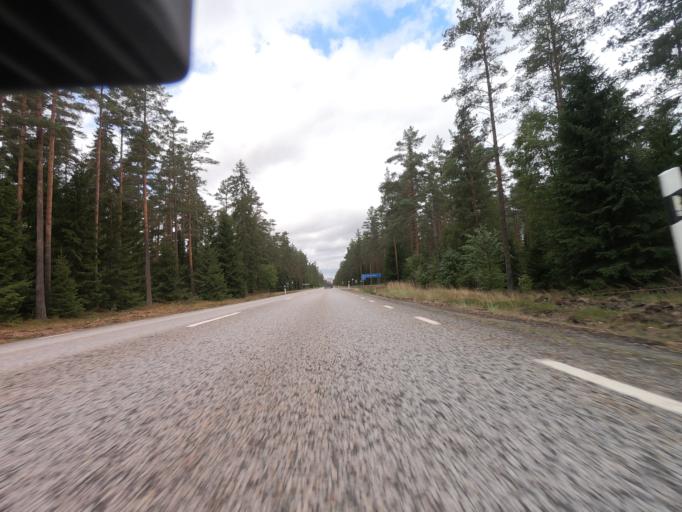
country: SE
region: Joenkoeping
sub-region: Vaggeryds Kommun
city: Vaggeryd
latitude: 57.5856
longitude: 14.2268
